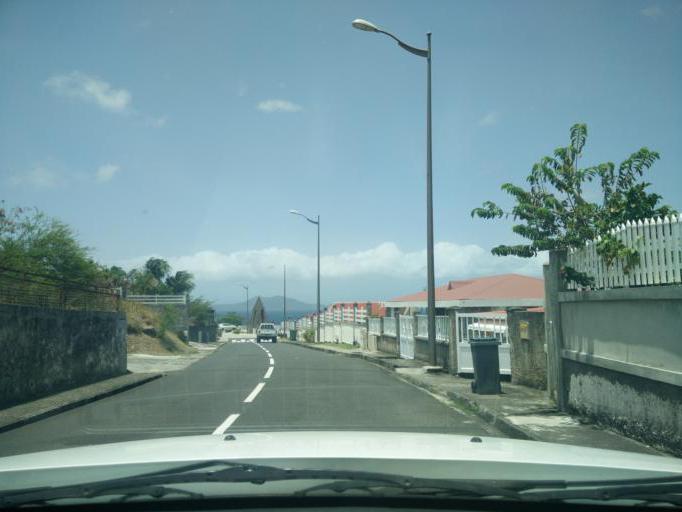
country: GP
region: Guadeloupe
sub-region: Guadeloupe
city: Gourbeyre
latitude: 15.9491
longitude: -61.6987
